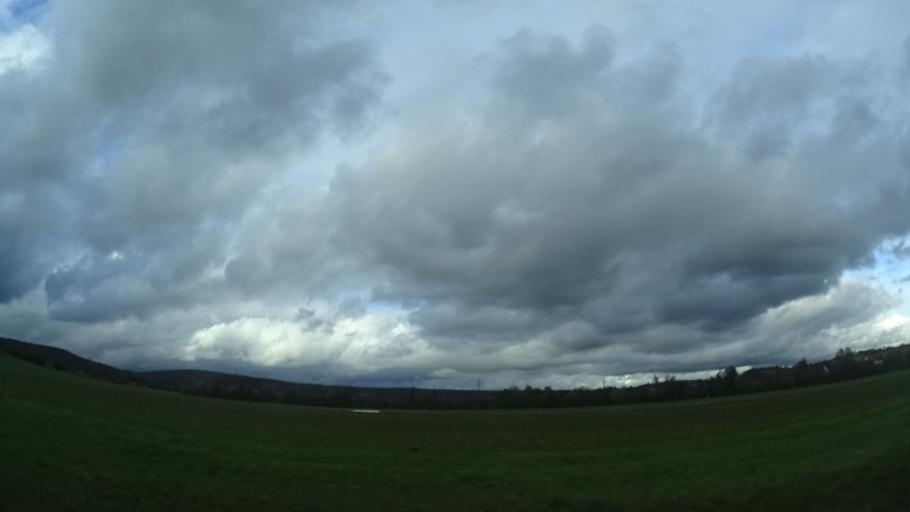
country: DE
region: Bavaria
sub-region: Regierungsbezirk Unterfranken
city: Hohenroth
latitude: 50.3300
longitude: 10.1878
